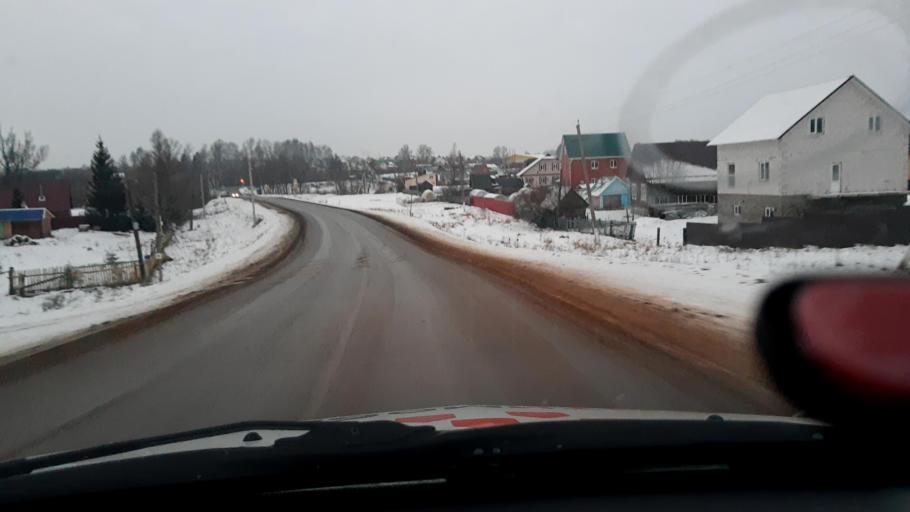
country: RU
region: Bashkortostan
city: Iglino
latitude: 54.8473
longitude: 56.4530
